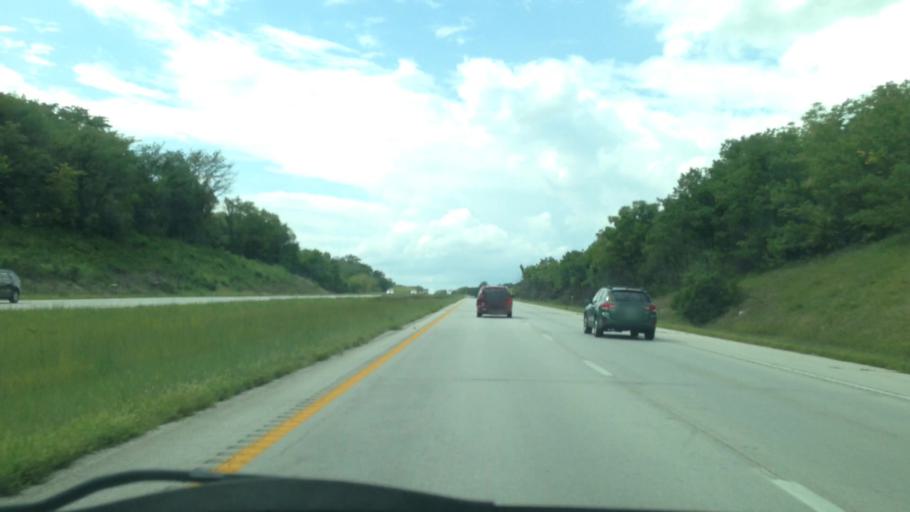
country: US
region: Missouri
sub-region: Marion County
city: Hannibal
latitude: 39.7382
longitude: -91.4136
